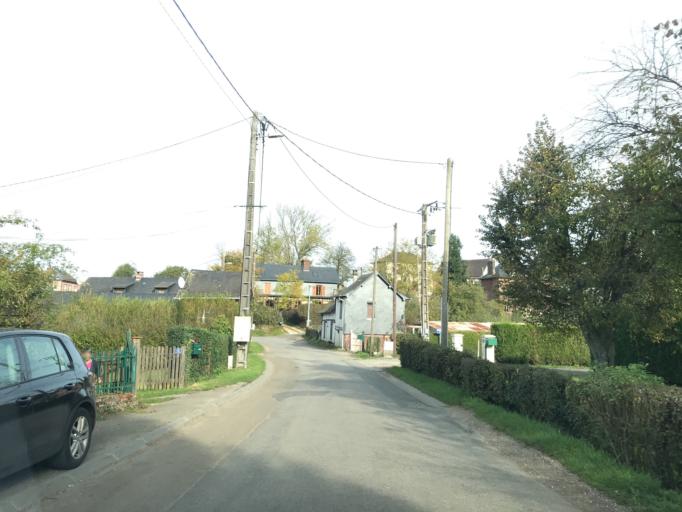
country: FR
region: Haute-Normandie
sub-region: Departement de l'Eure
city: Perriers-sur-Andelle
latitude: 49.4615
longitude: 1.3975
